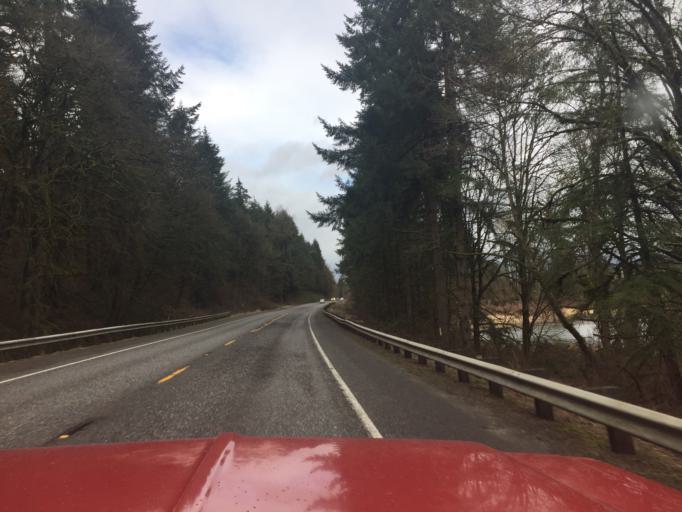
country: US
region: Washington
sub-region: Cowlitz County
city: Kalama
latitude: 45.9829
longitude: -122.8703
